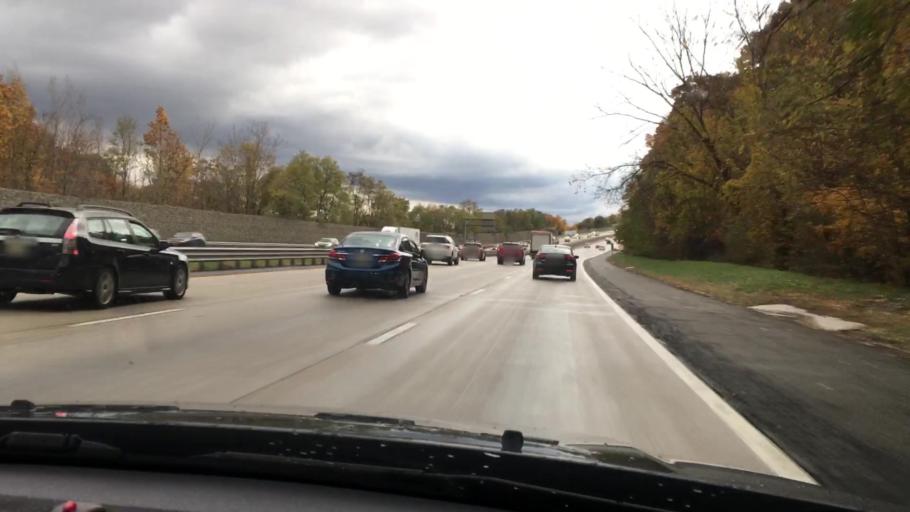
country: US
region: New Jersey
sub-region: Morris County
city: Riverdale
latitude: 40.9757
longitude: -74.3193
